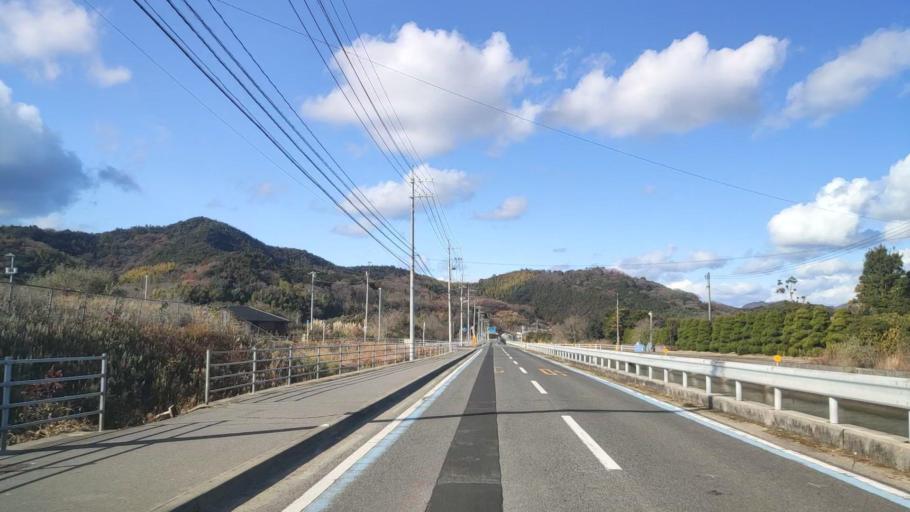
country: JP
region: Hiroshima
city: Innoshima
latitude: 34.2143
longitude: 133.1090
